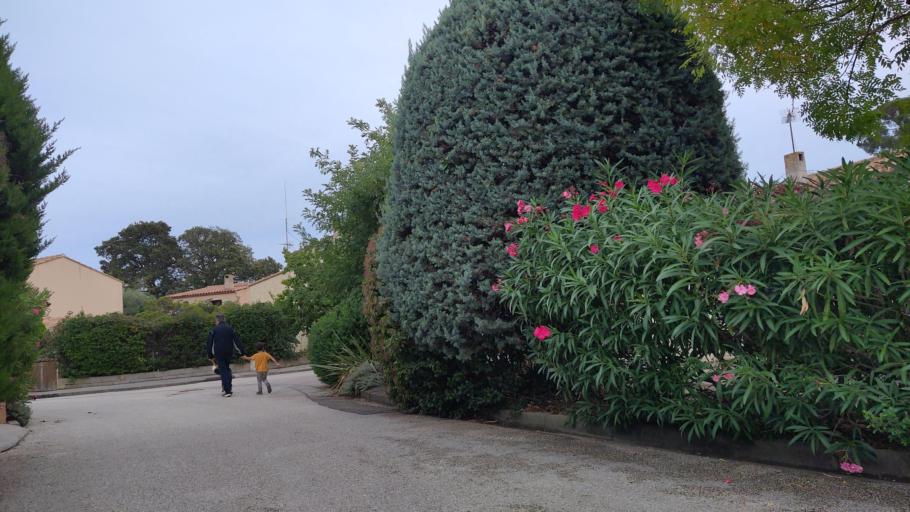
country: FR
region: Provence-Alpes-Cote d'Azur
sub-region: Departement du Var
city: Sanary-sur-Mer
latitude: 43.1252
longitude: 5.8007
